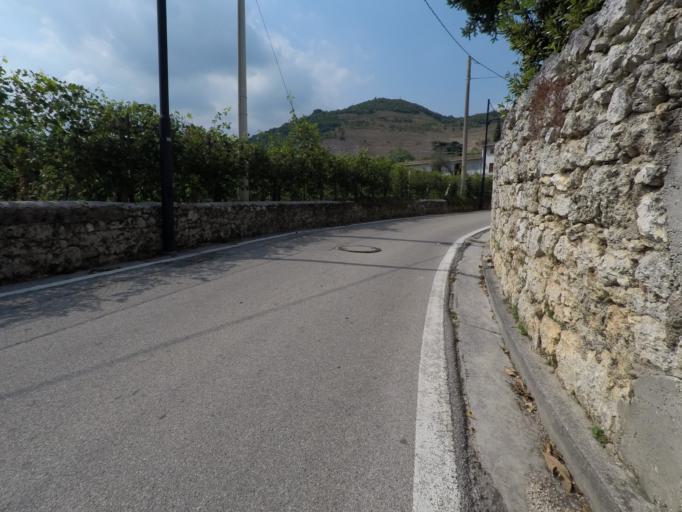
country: IT
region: Friuli Venezia Giulia
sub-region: Provincia di Pordenone
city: Caneva
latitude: 45.9677
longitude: 12.4298
